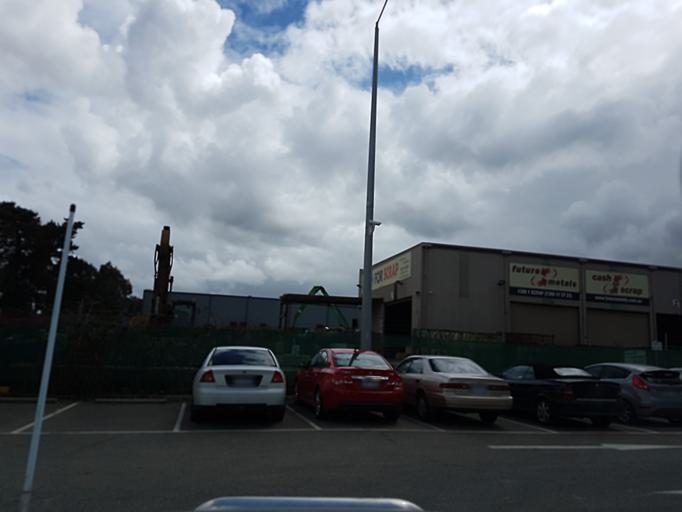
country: AU
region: Victoria
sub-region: Casey
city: Hallam
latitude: -38.0175
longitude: 145.2686
